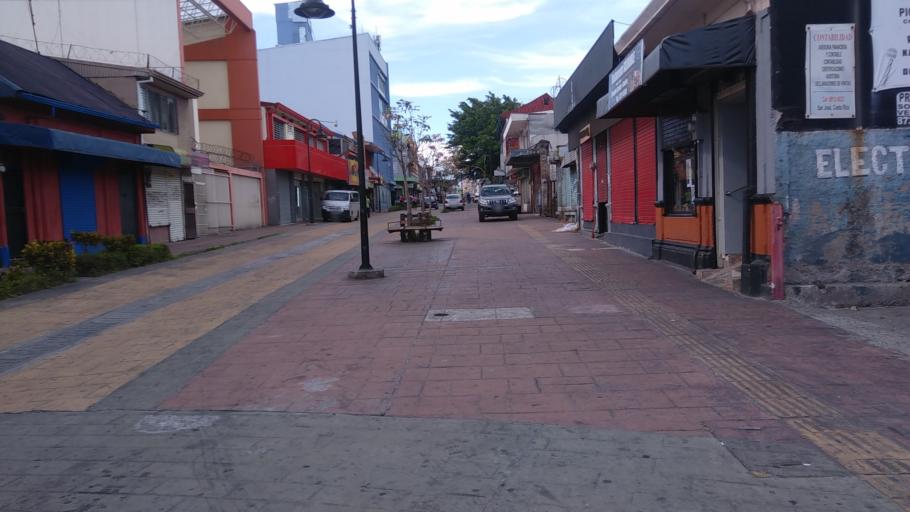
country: CR
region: San Jose
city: San Jose
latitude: 9.9286
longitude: -84.0753
